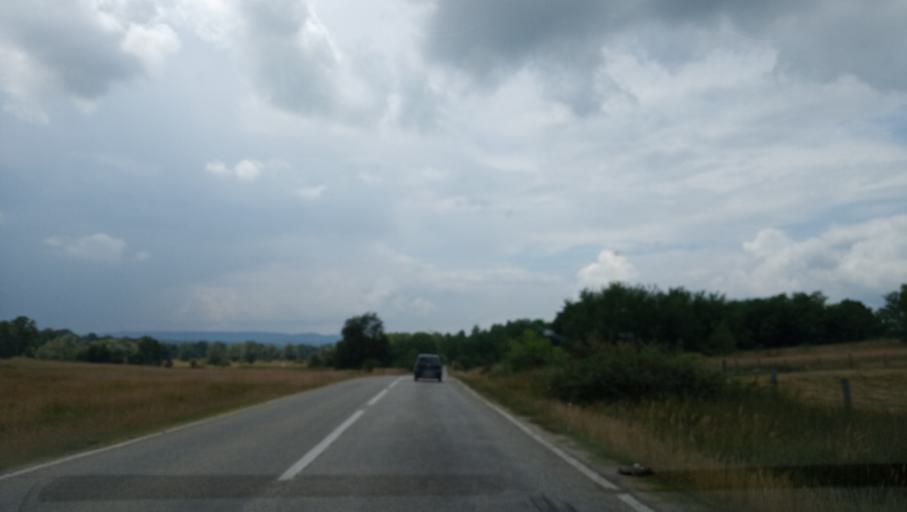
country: RO
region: Gorj
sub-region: Comuna Tismana
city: Tismana
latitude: 45.0400
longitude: 22.9840
